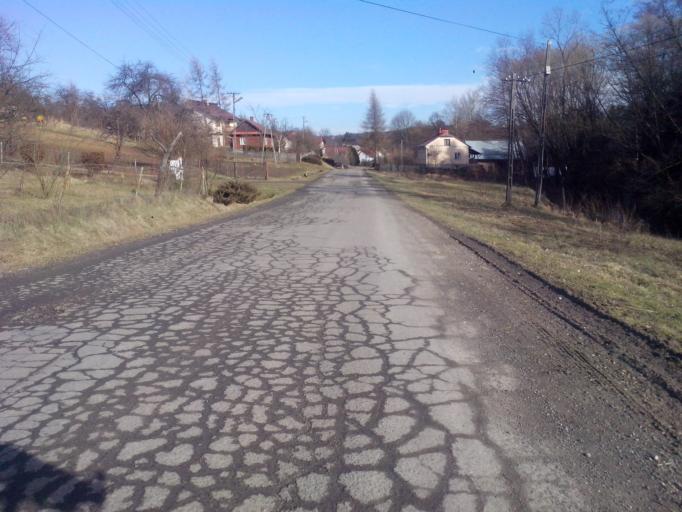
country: PL
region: Subcarpathian Voivodeship
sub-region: Powiat strzyzowski
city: Strzyzow
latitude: 49.8118
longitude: 21.8286
